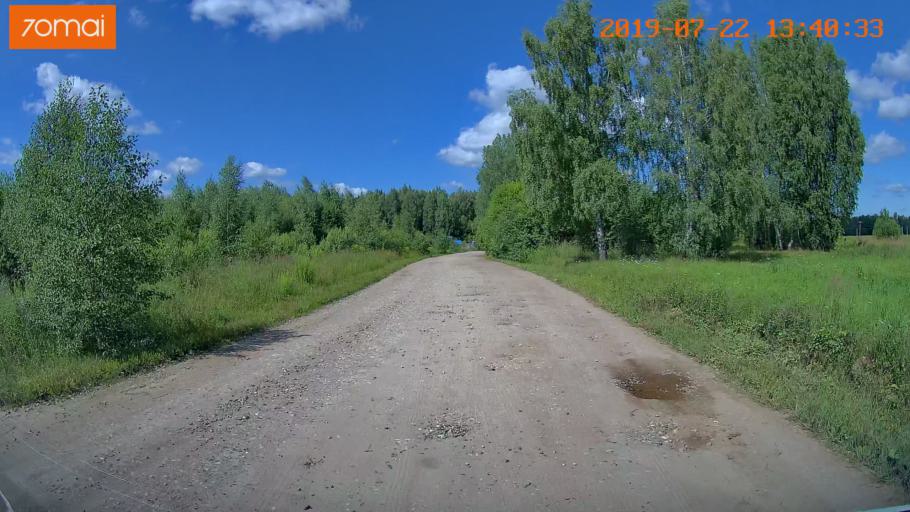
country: RU
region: Ivanovo
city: Novo-Talitsy
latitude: 57.0767
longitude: 40.8810
